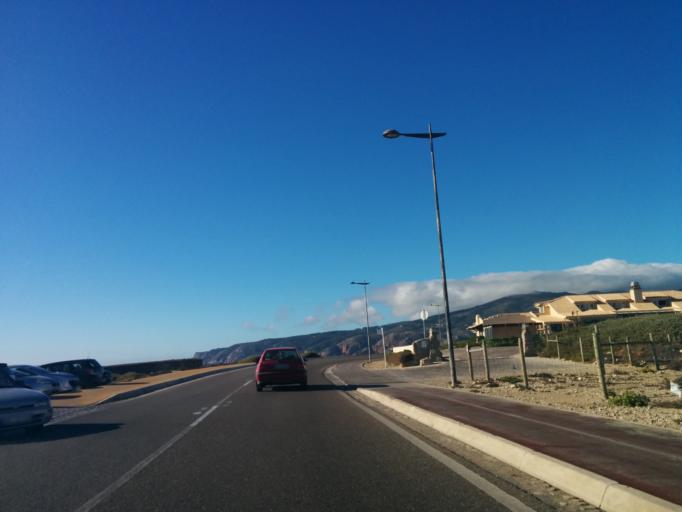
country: PT
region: Lisbon
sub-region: Cascais
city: Cascais
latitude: 38.7217
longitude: -9.4778
